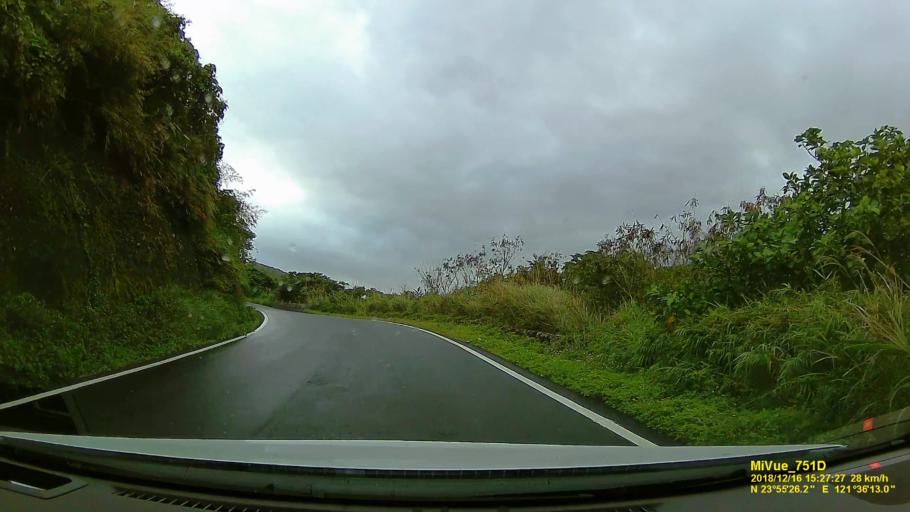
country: TW
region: Taiwan
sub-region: Hualien
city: Hualian
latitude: 23.9238
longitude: 121.6034
